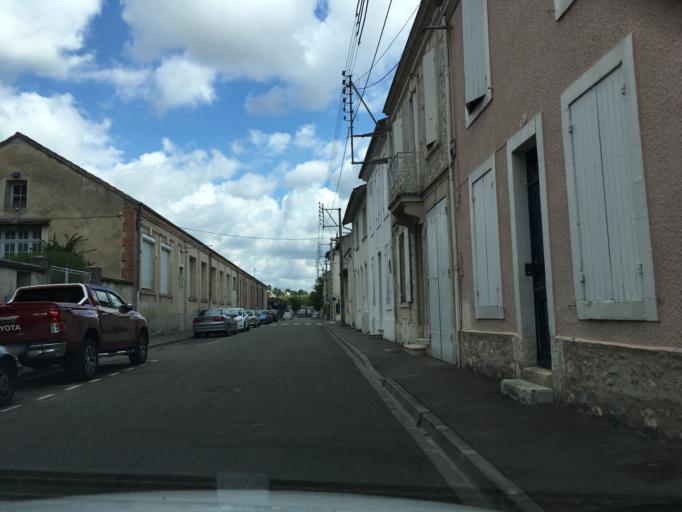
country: FR
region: Aquitaine
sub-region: Departement du Lot-et-Garonne
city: Agen
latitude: 44.2029
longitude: 0.6305
